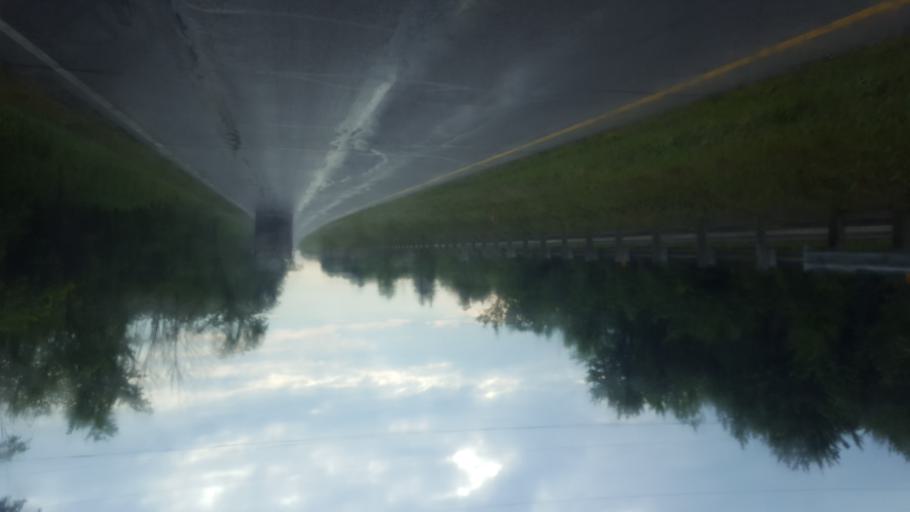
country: US
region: Ohio
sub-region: Portage County
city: Hiram
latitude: 41.3752
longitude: -81.1032
